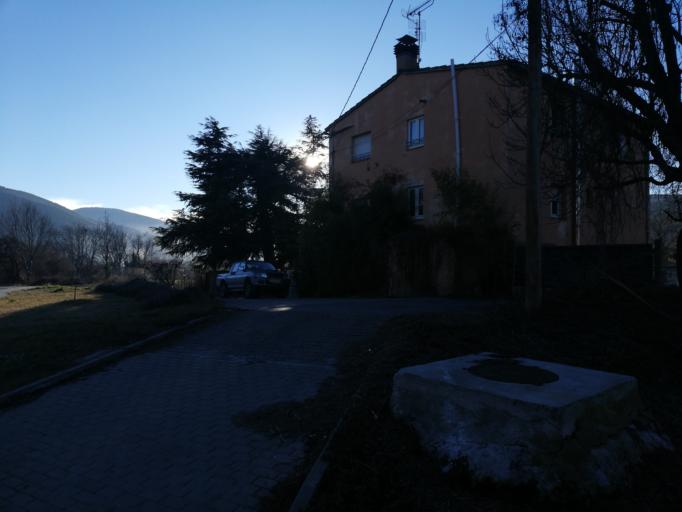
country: ES
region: Catalonia
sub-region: Provincia de Lleida
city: la Seu d'Urgell
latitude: 42.3531
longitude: 1.4518
